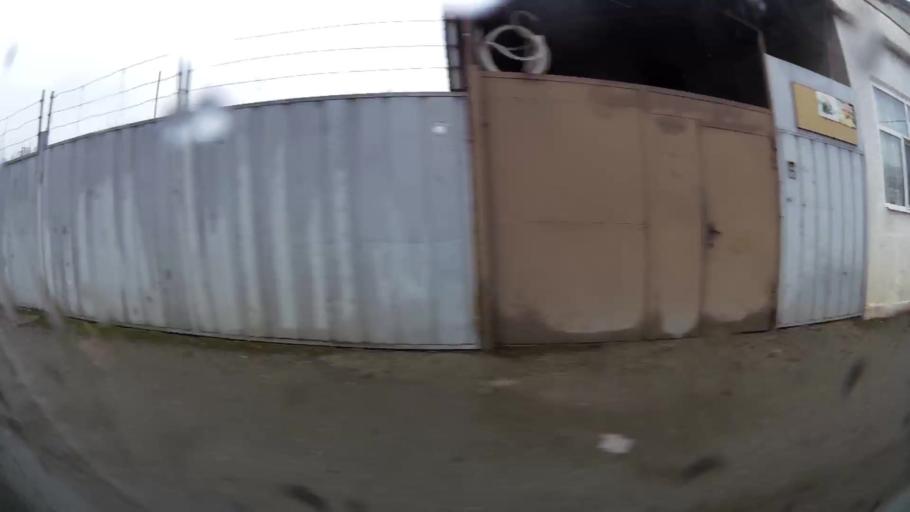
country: BG
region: Sofia-Capital
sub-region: Stolichna Obshtina
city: Sofia
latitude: 42.6637
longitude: 23.4228
